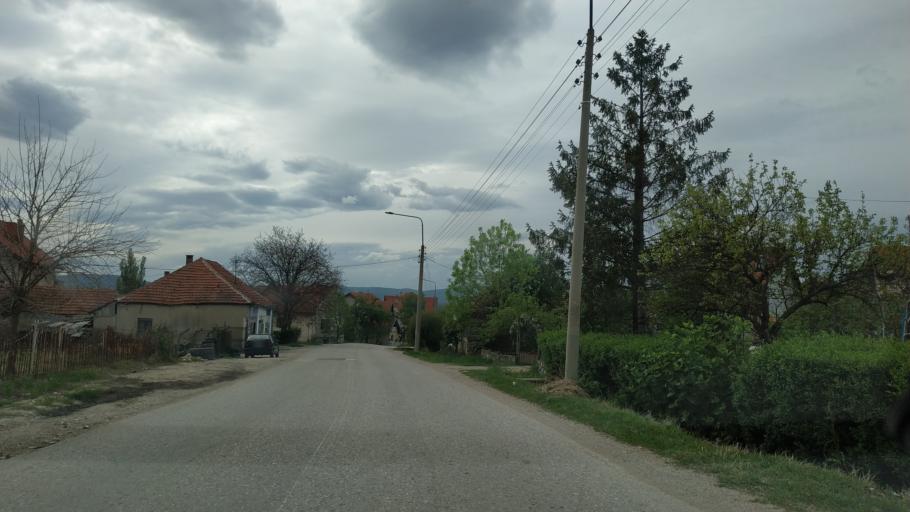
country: RS
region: Central Serbia
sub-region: Zajecarski Okrug
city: Soko Banja
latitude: 43.6454
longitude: 21.8858
